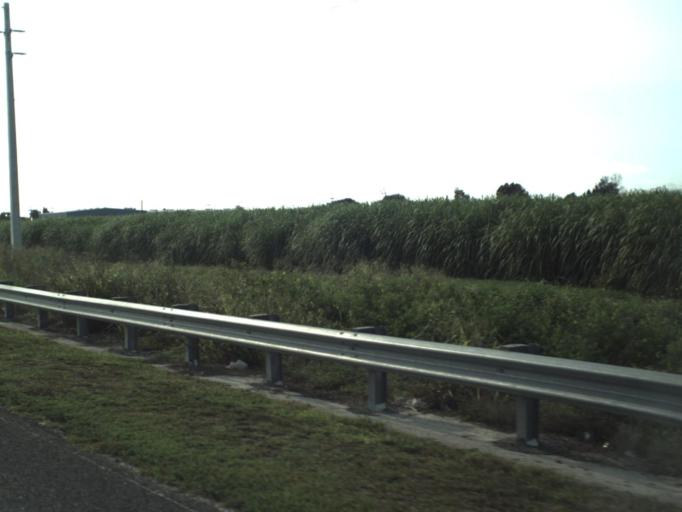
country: US
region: Florida
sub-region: Palm Beach County
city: South Bay
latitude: 26.6802
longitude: -80.7341
